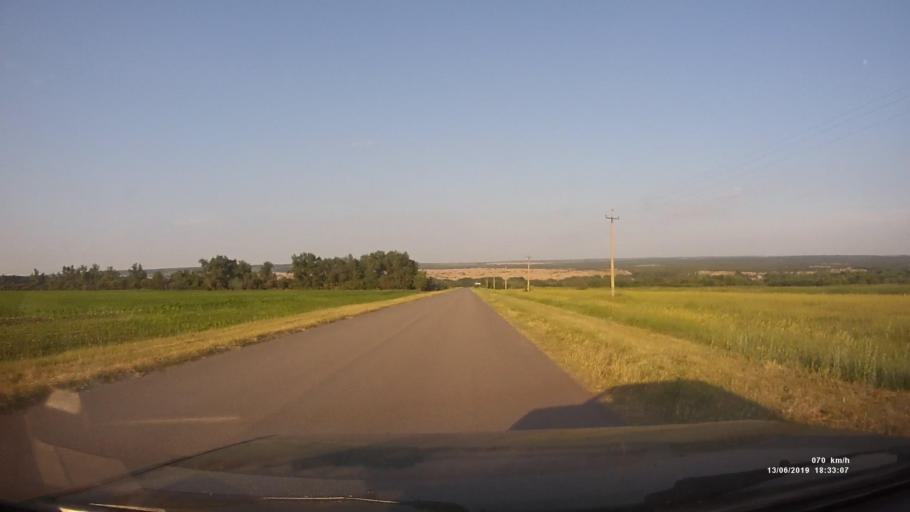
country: RU
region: Rostov
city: Kazanskaya
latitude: 49.8703
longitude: 41.3775
